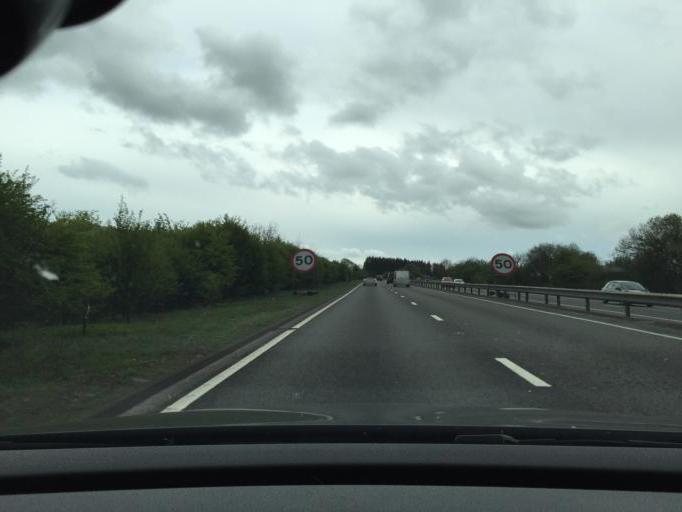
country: GB
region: England
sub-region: West Berkshire
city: Hermitage
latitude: 51.5151
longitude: -1.2905
